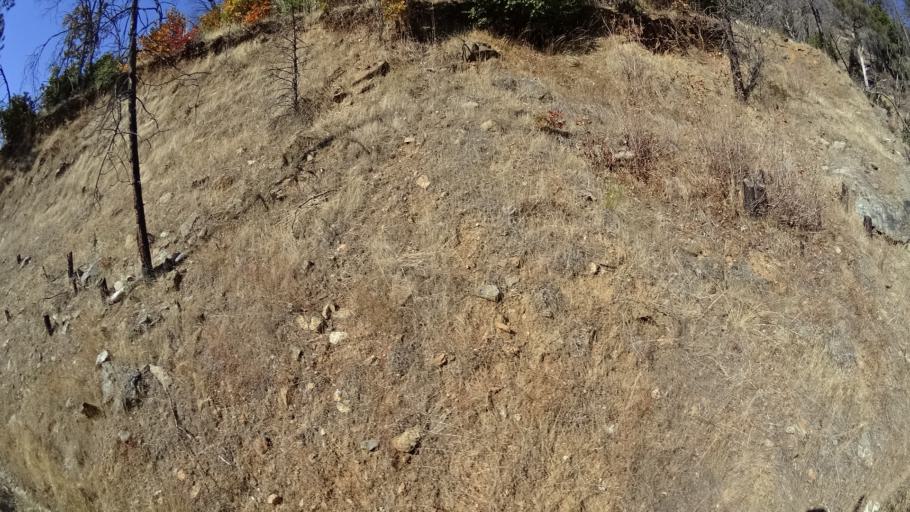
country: US
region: California
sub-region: Siskiyou County
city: Happy Camp
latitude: 41.7073
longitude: -123.0327
